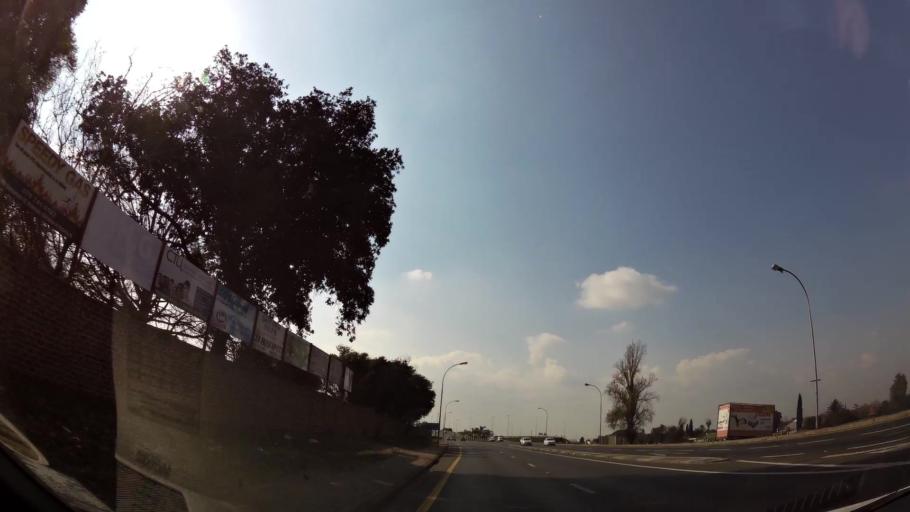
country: ZA
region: Gauteng
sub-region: Ekurhuleni Metropolitan Municipality
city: Germiston
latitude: -26.1775
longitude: 28.1943
